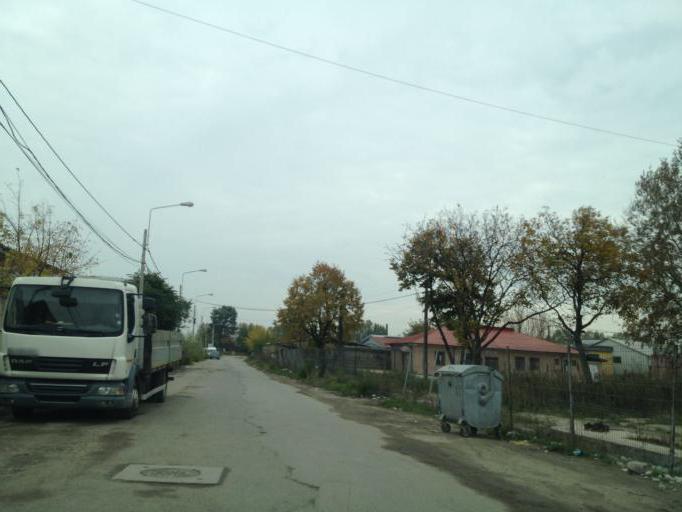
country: RO
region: Dolj
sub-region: Municipiul Craiova
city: Popoveni
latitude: 44.2953
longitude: 23.7929
